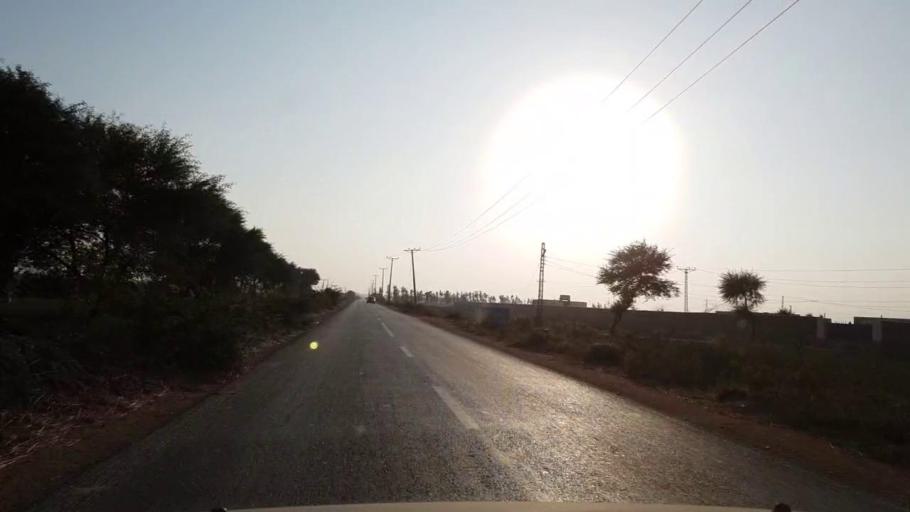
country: PK
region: Sindh
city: Daro Mehar
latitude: 24.6265
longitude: 68.1006
